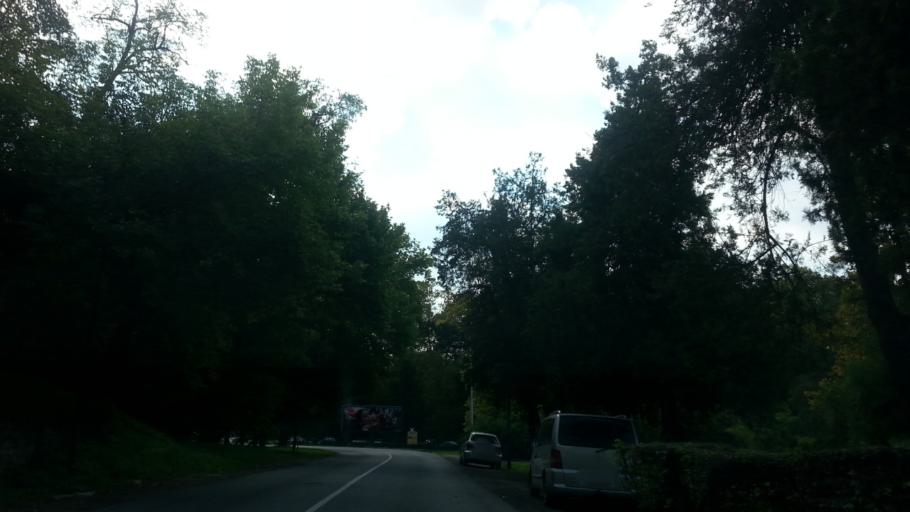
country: RS
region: Central Serbia
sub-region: Belgrade
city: Savski Venac
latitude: 44.7804
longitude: 20.4425
